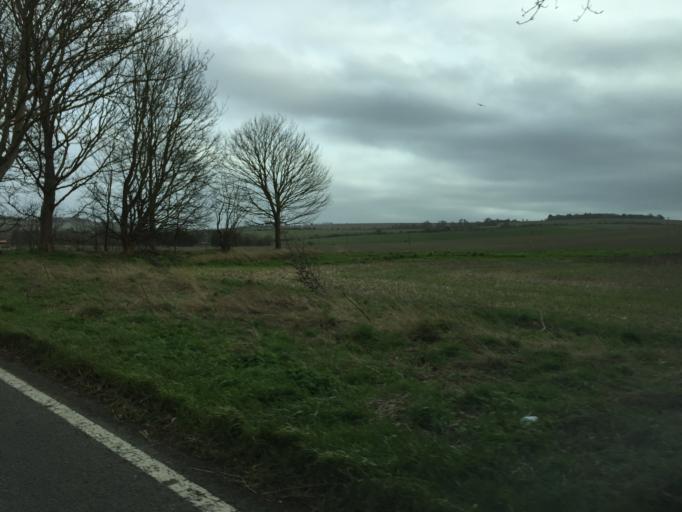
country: GB
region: England
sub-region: Oxfordshire
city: Blewbury
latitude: 51.5707
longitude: -1.2507
